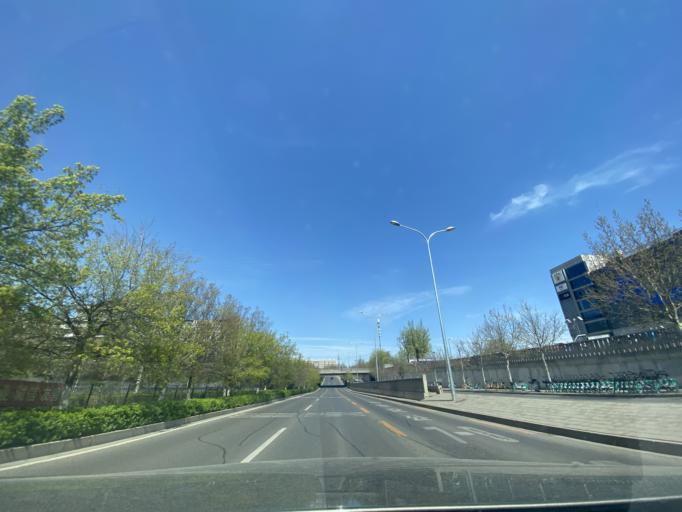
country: CN
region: Beijing
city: Sijiqing
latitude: 39.9300
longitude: 116.2470
